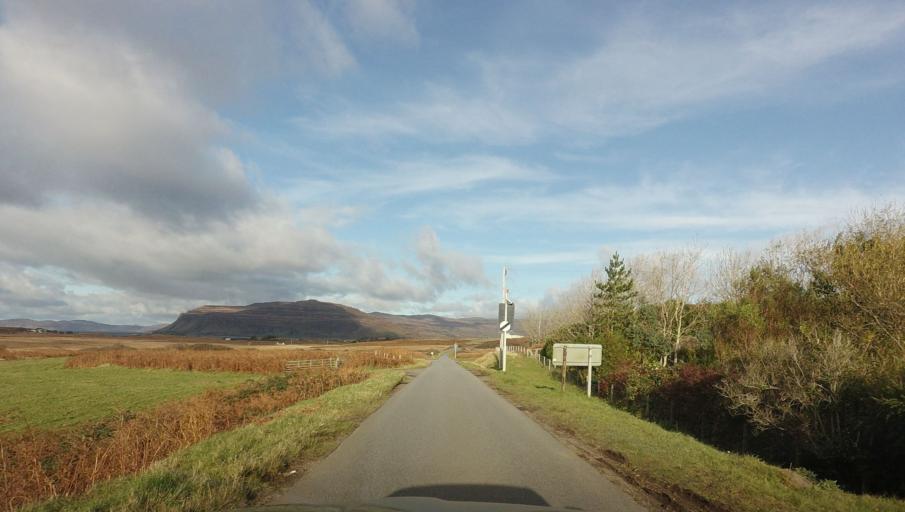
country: GB
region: Scotland
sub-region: Argyll and Bute
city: Isle Of Mull
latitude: 56.3188
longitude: -6.2190
